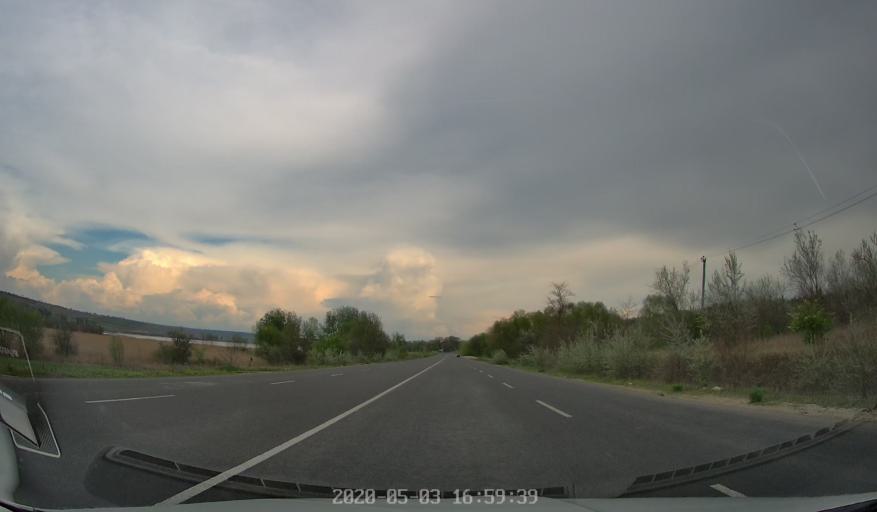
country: MD
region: Straseni
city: Straseni
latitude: 47.1231
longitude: 28.6704
